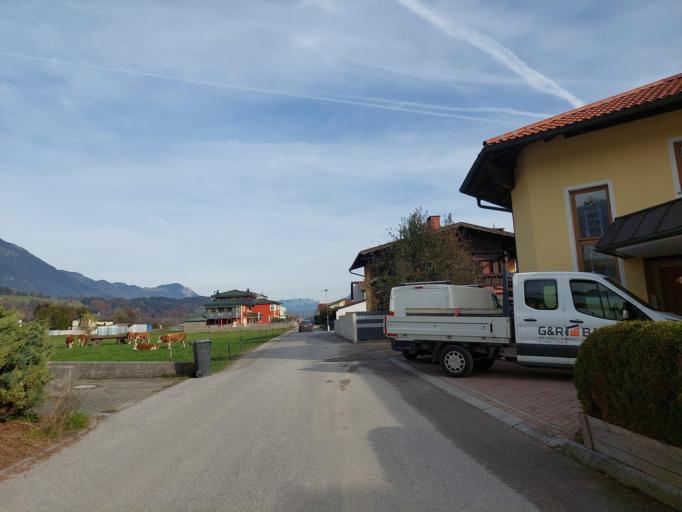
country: AT
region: Tyrol
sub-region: Politischer Bezirk Kufstein
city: Radfeld
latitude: 47.4501
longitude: 11.9101
